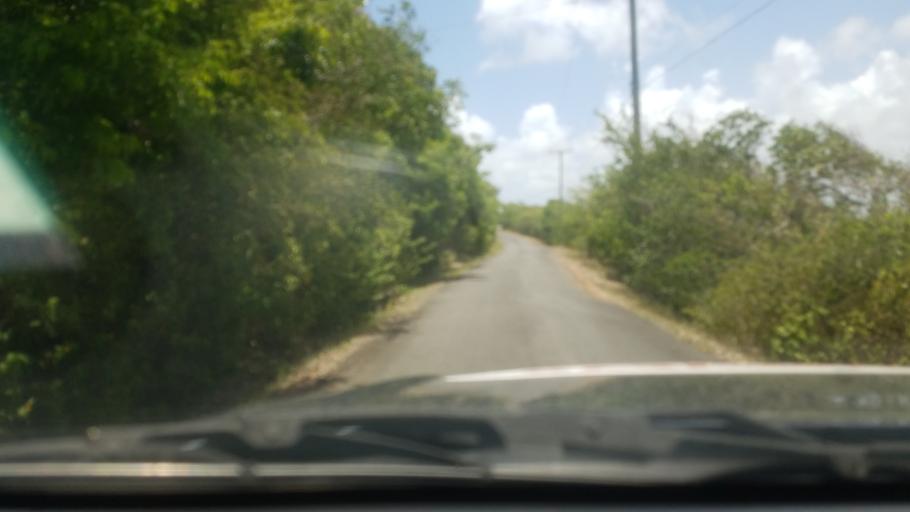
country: LC
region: Vieux-Fort
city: Vieux Fort
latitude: 13.7130
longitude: -60.9462
